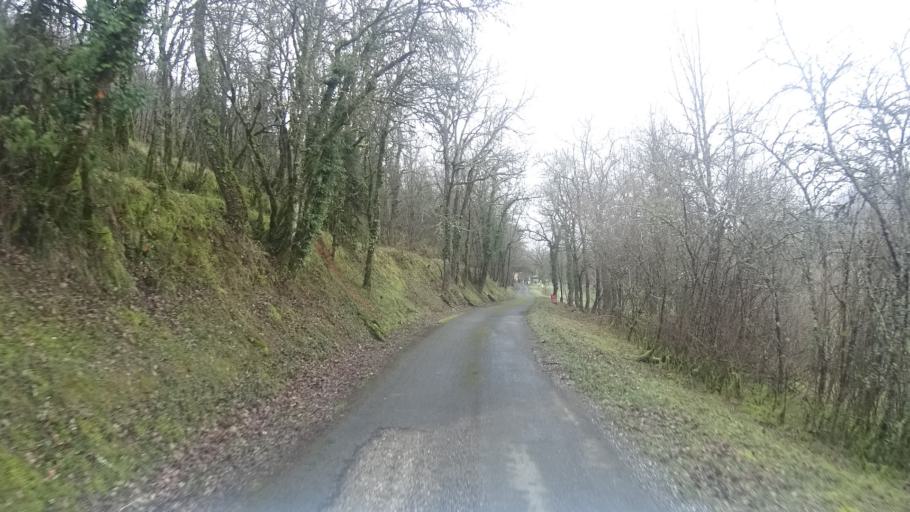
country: FR
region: Aquitaine
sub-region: Departement de la Dordogne
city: Terrasson-Lavilledieu
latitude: 45.1124
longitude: 1.2358
